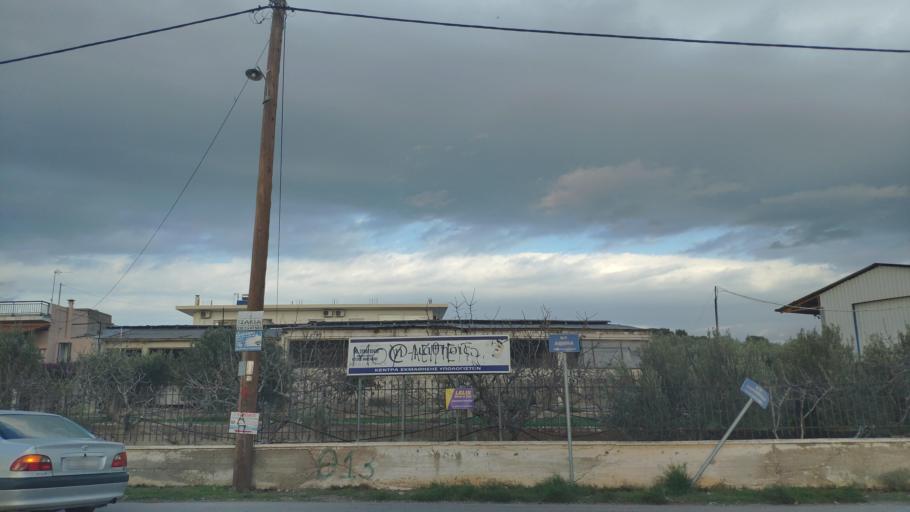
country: GR
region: Attica
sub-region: Nomarchia Dytikis Attikis
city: Nea Peramos
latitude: 37.9938
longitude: 23.3970
